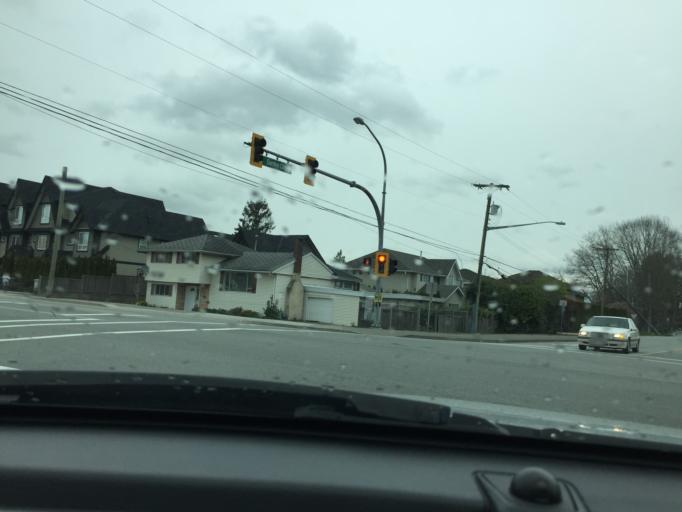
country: CA
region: British Columbia
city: Richmond
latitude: 49.1407
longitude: -123.1252
